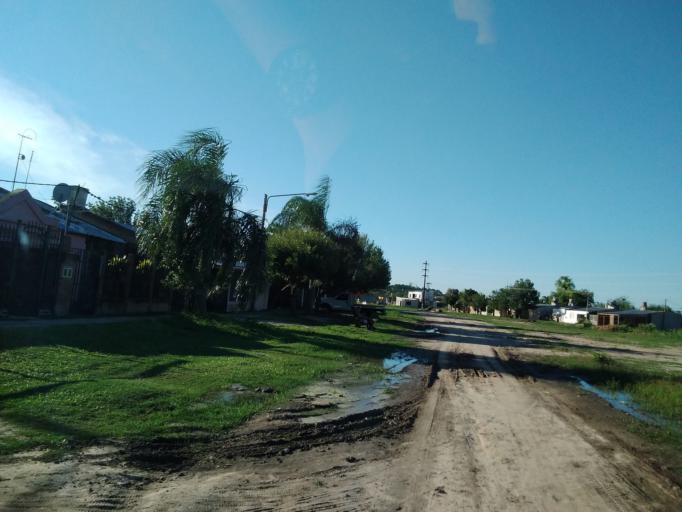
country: AR
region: Corrientes
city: Corrientes
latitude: -27.5079
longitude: -58.7780
